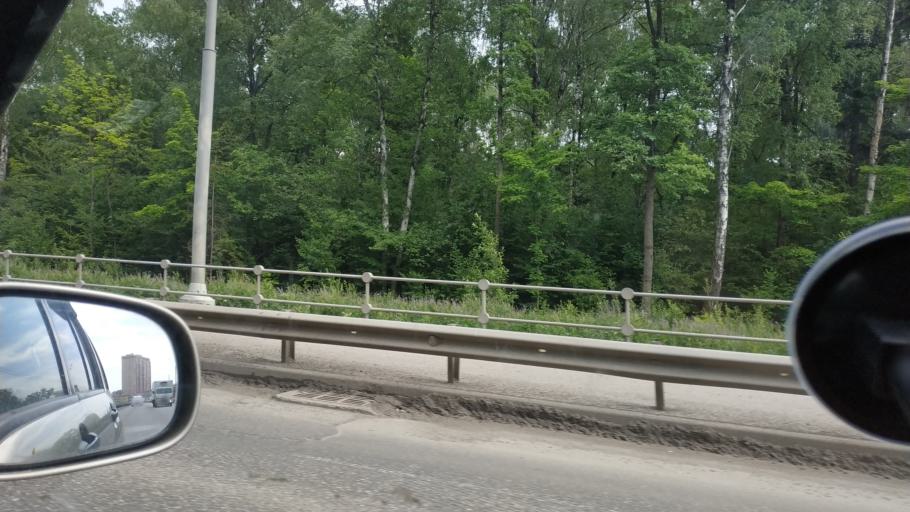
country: RU
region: Moskovskaya
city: Fryazino
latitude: 55.9428
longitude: 38.0373
